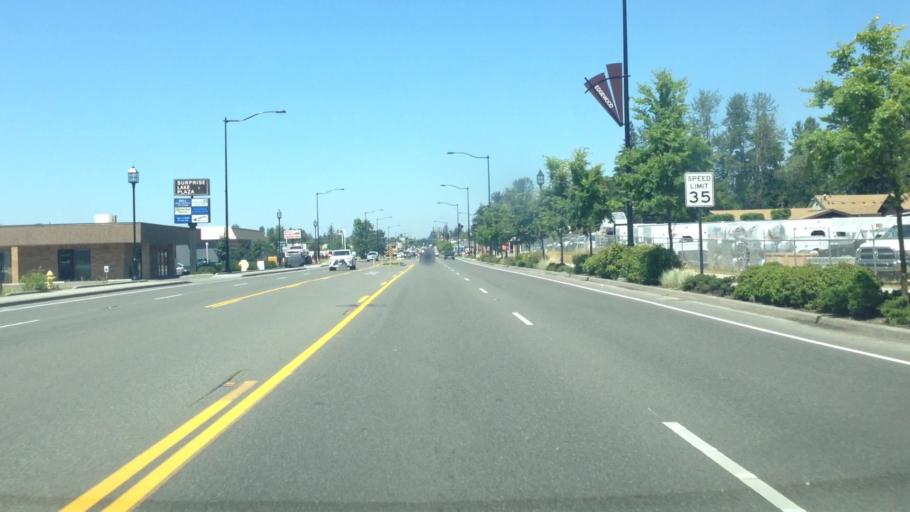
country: US
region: Washington
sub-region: Pierce County
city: Edgewood
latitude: 47.2433
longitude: -122.2939
